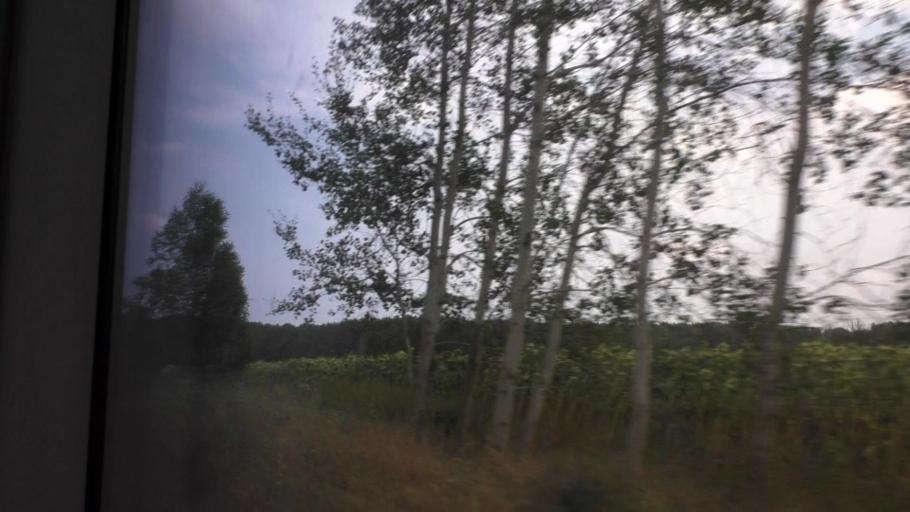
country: DE
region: Brandenburg
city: Mixdorf
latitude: 52.1925
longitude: 14.3912
